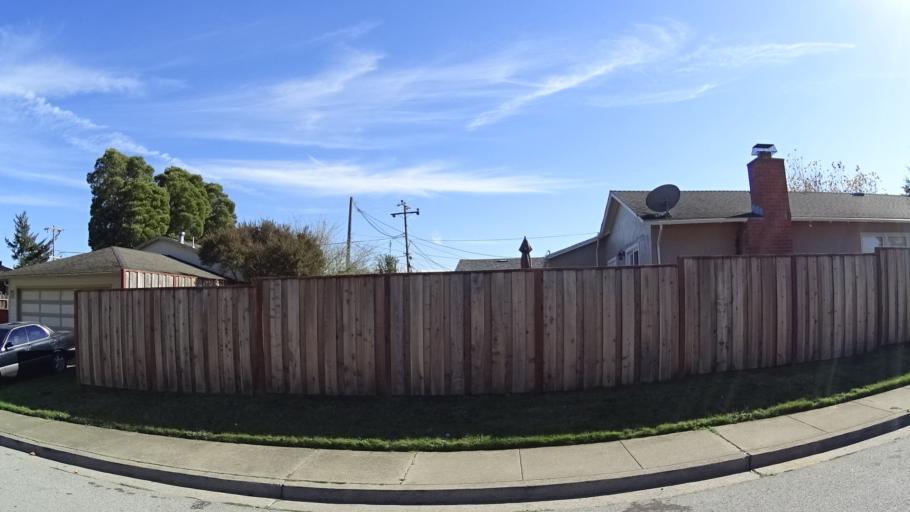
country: US
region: California
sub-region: San Mateo County
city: Pacifica
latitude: 37.6323
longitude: -122.4523
